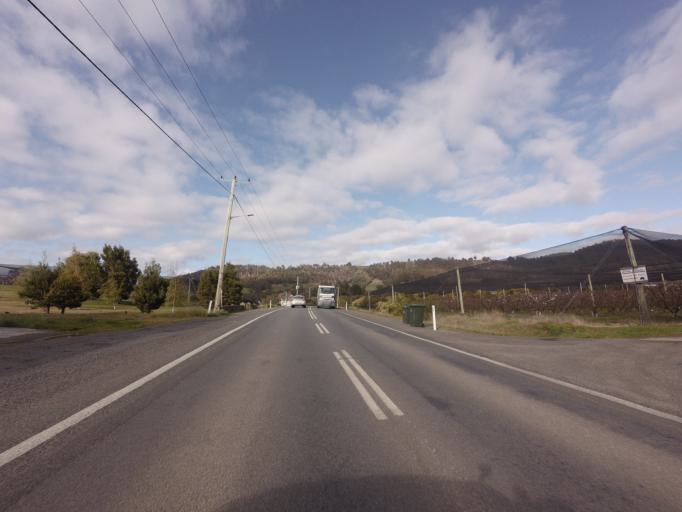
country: AU
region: Tasmania
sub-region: Huon Valley
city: Geeveston
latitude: -43.1353
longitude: 146.9747
